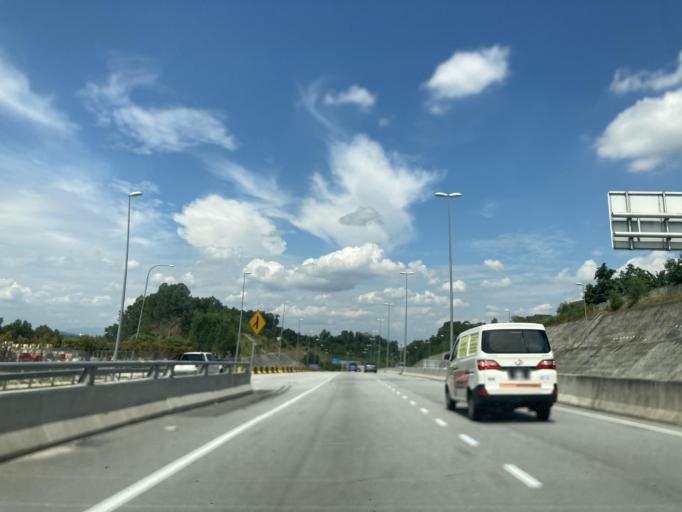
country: MY
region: Selangor
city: Kampung Baru Subang
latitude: 3.1266
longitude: 101.5218
